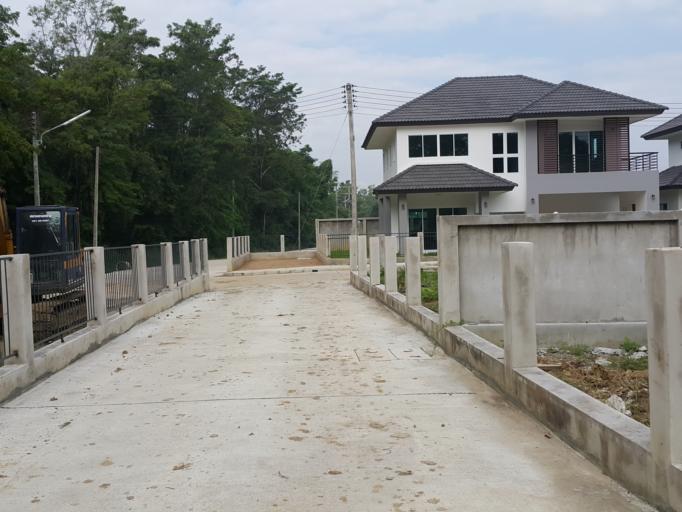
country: TH
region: Chiang Mai
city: San Kamphaeng
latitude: 18.7603
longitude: 99.1024
